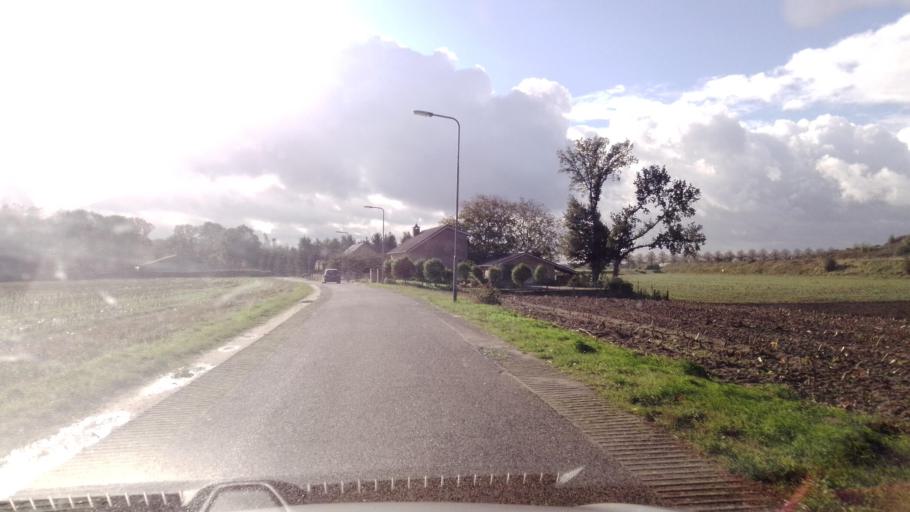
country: NL
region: Limburg
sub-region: Gemeente Venlo
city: Arcen
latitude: 51.4407
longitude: 6.1686
